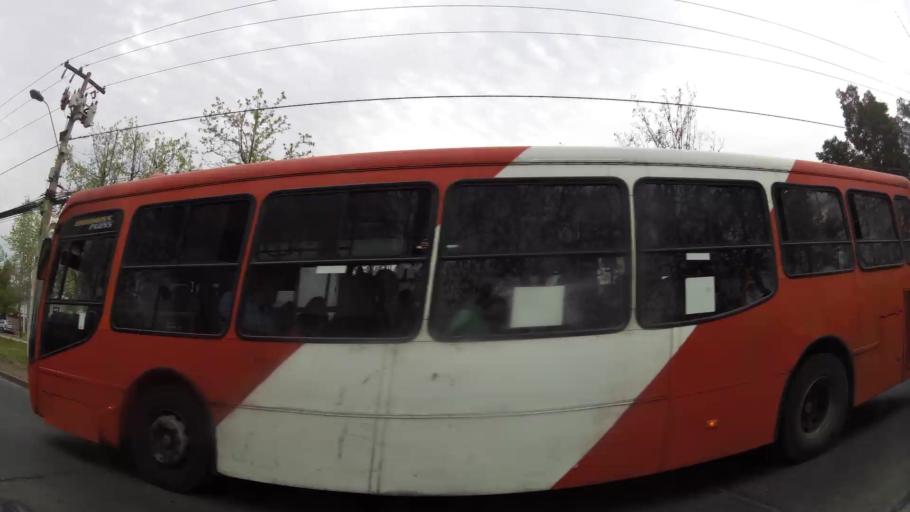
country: CL
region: Santiago Metropolitan
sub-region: Provincia de Santiago
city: Villa Presidente Frei, Nunoa, Santiago, Chile
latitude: -33.4744
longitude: -70.6128
